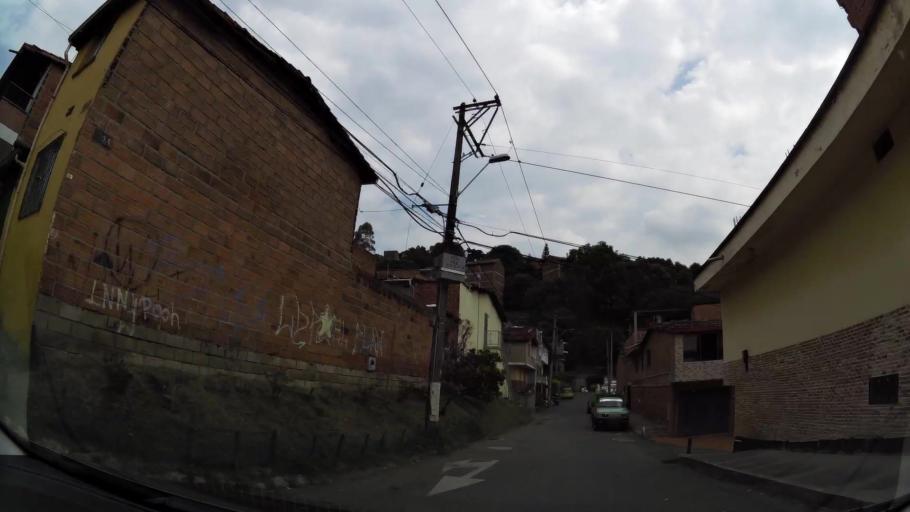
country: CO
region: Antioquia
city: Itagui
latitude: 6.1977
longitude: -75.5933
